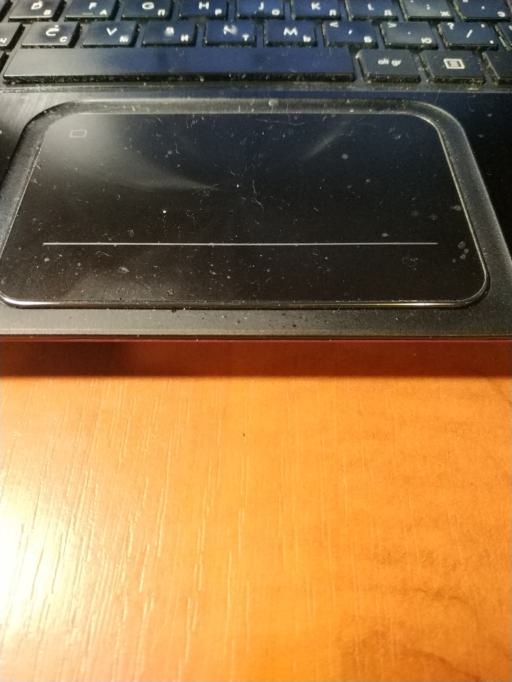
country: RU
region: Nizjnij Novgorod
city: Kulebaki
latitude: 55.5319
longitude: 42.6693
